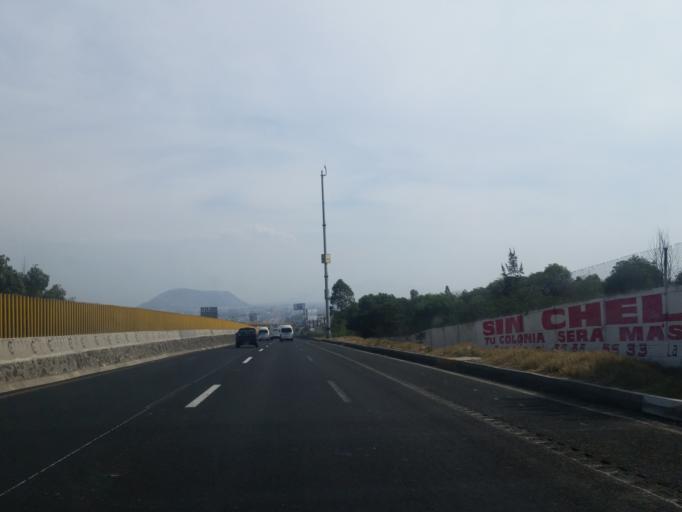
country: MX
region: Mexico
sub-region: La Paz
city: Emiliano Zapata
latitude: 19.3357
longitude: -98.9729
